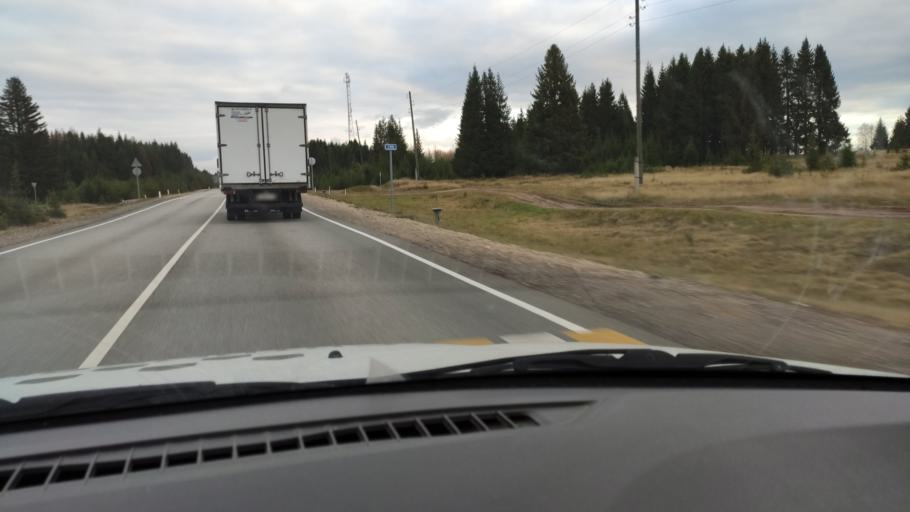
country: RU
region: Kirov
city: Chernaya Kholunitsa
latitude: 58.8569
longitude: 51.7210
